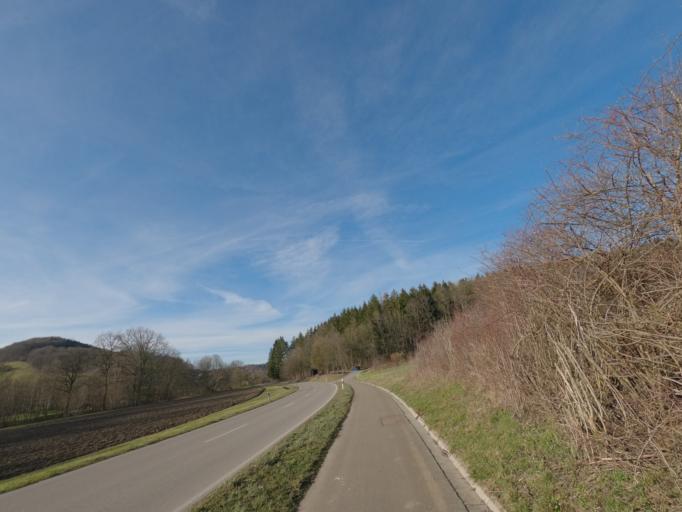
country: DE
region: Baden-Wuerttemberg
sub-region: Regierungsbezirk Stuttgart
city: Donzdorf
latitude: 48.7006
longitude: 9.8005
